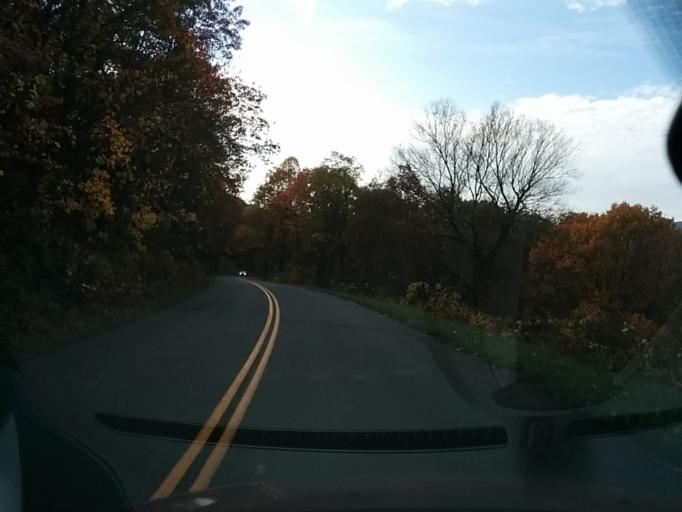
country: US
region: Virginia
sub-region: Augusta County
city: Stuarts Draft
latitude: 37.8947
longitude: -79.0366
